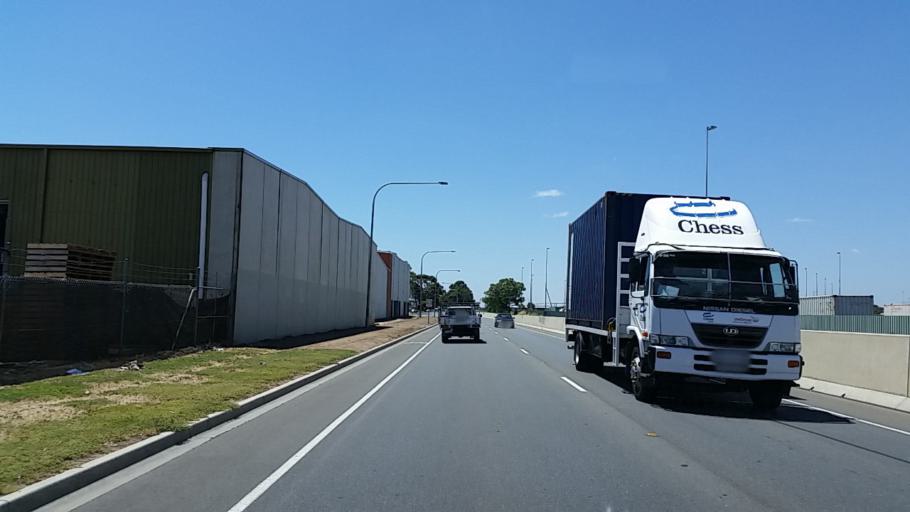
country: AU
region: South Australia
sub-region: Port Adelaide Enfield
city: Blair Athol
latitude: -34.8673
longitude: 138.5748
